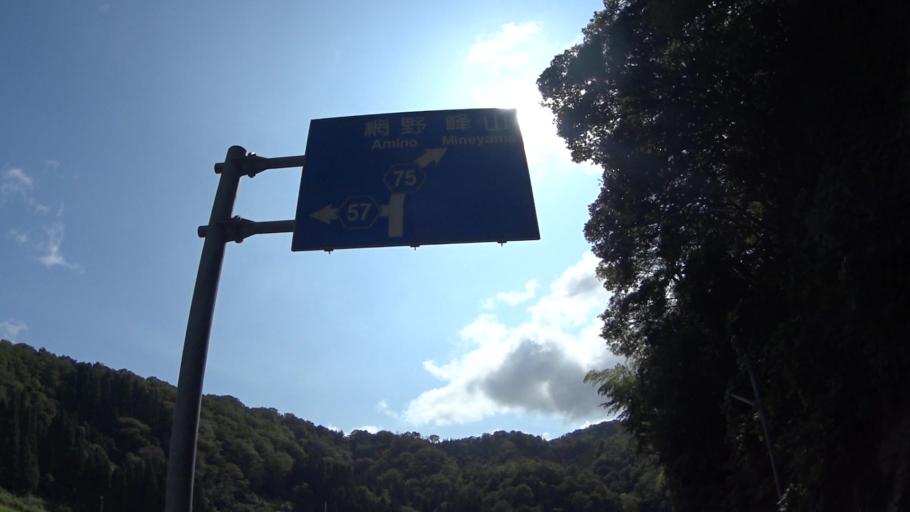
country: JP
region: Kyoto
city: Miyazu
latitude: 35.6851
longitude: 135.1550
